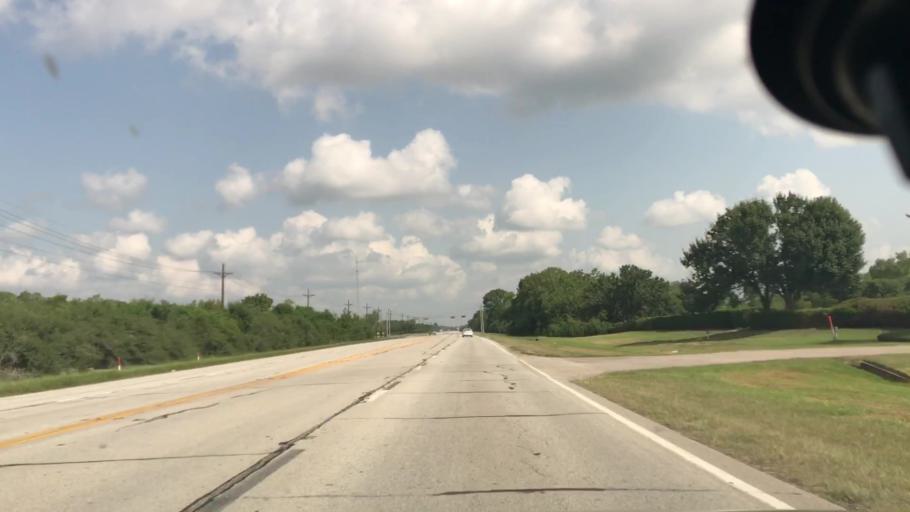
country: US
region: Texas
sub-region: Brazoria County
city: Angleton
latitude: 29.2063
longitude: -95.4358
